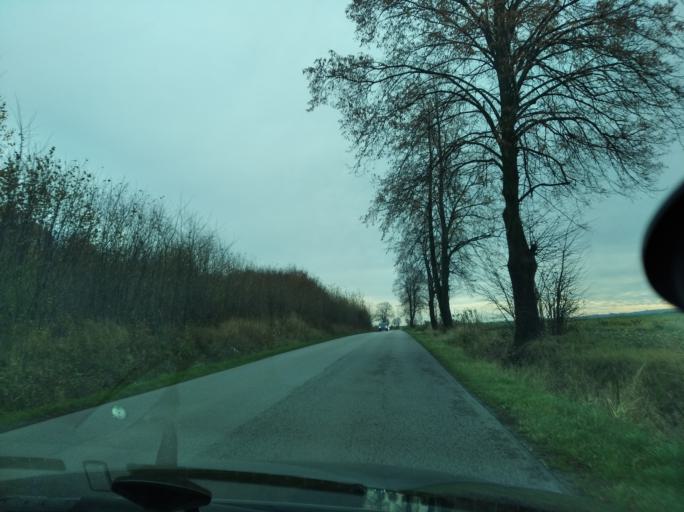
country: PL
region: Subcarpathian Voivodeship
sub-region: Powiat lancucki
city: Wysoka
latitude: 50.0272
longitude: 22.2489
